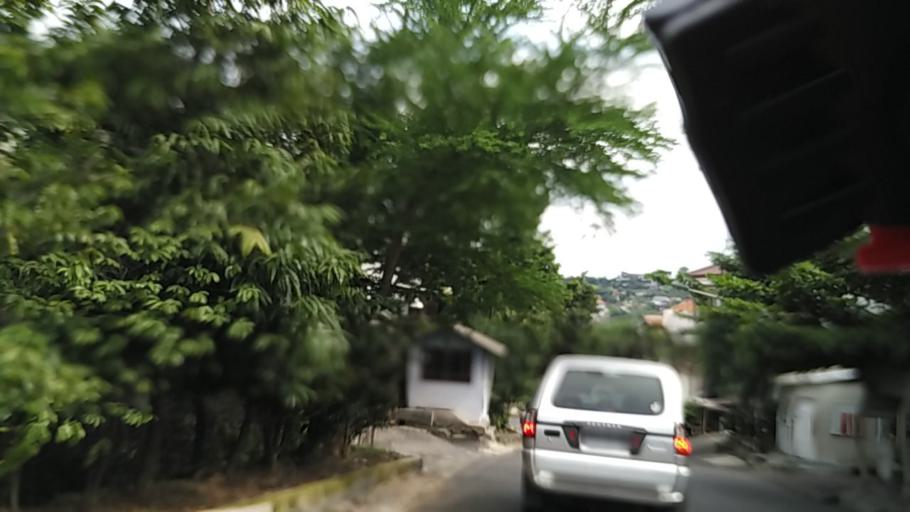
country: ID
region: Central Java
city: Semarang
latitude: -7.0100
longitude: 110.4260
